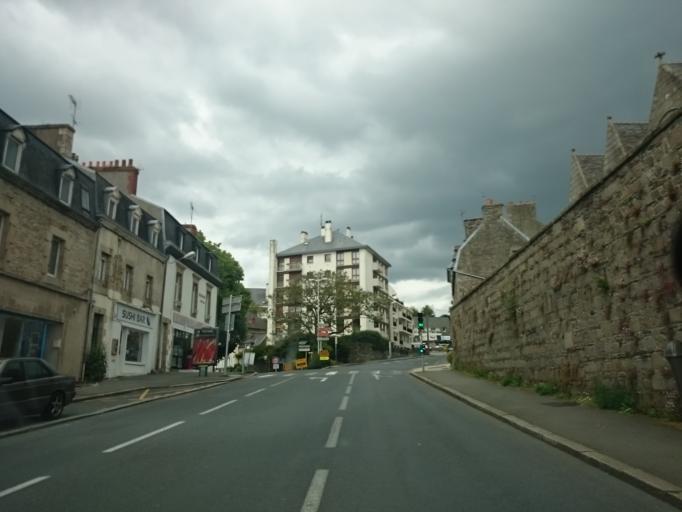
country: FR
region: Brittany
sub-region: Departement des Cotes-d'Armor
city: Lannion
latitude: 48.7328
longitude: -3.4605
